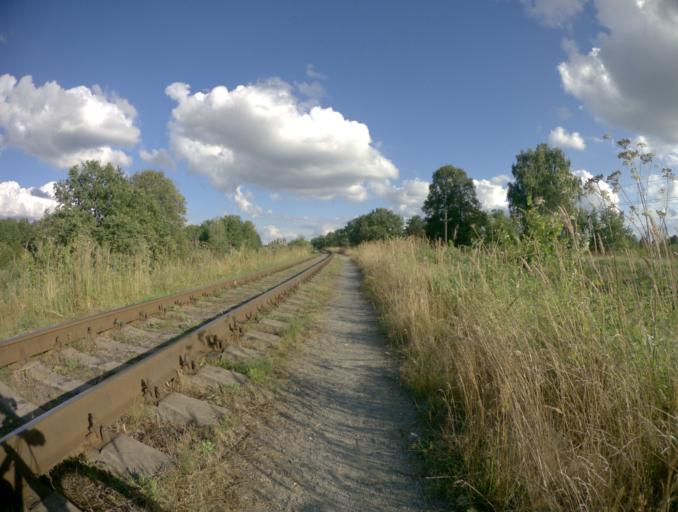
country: RU
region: Vladimir
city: Raduzhnyy
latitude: 56.0565
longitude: 40.3695
